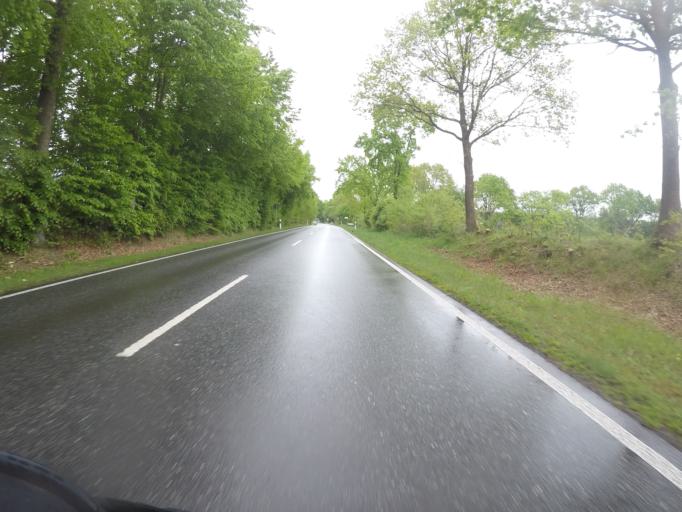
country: DE
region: Schleswig-Holstein
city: Heidmuhlen
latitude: 53.9530
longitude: 10.0852
